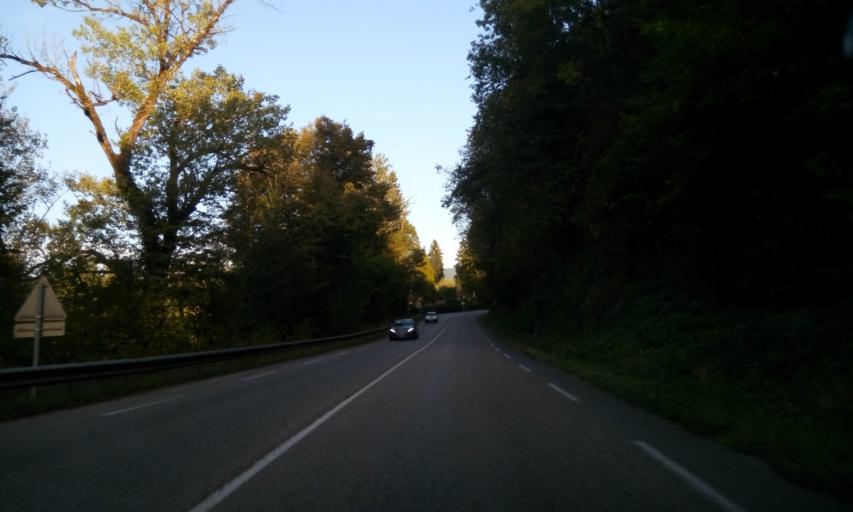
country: FR
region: Rhone-Alpes
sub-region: Departement de l'Ain
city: Poncin
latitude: 46.0844
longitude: 5.3985
